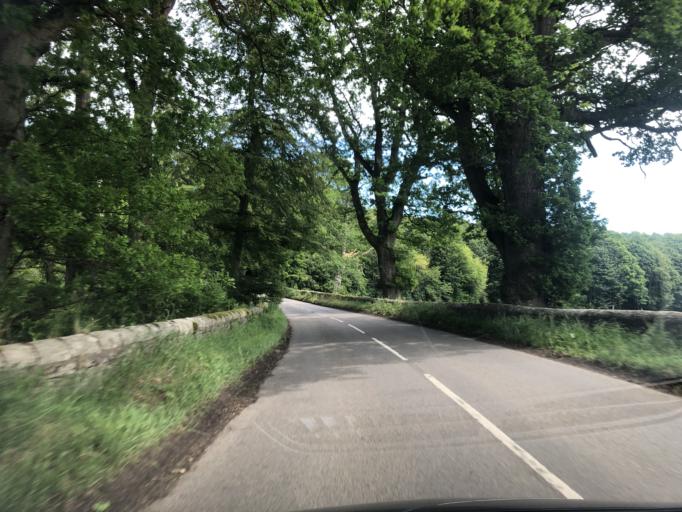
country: GB
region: Scotland
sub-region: Angus
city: Kirriemuir
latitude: 56.7160
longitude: -2.9891
